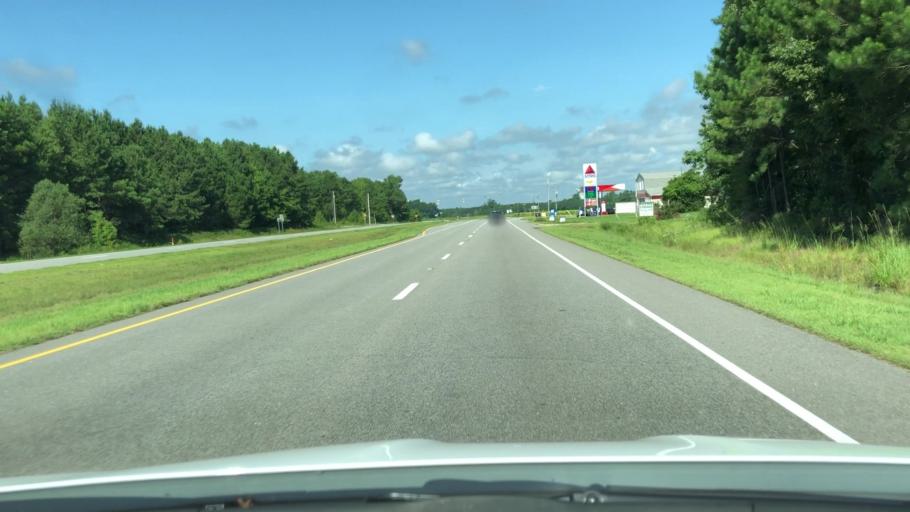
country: US
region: North Carolina
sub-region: Chowan County
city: Edenton
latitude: 36.0379
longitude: -76.7363
